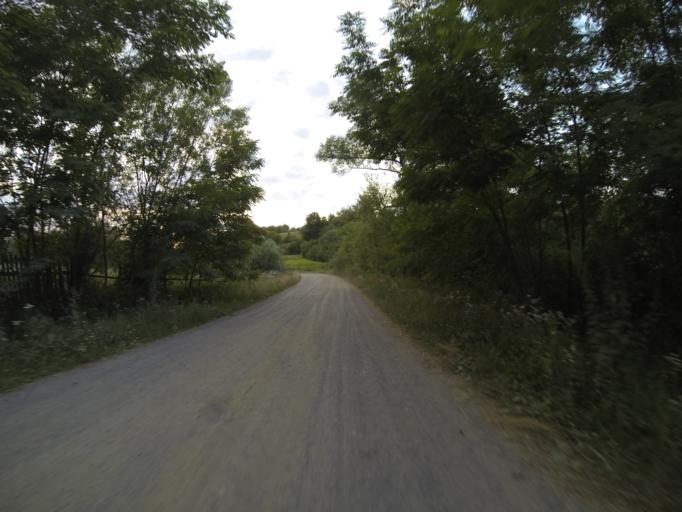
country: RO
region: Brasov
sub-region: Comuna Sinca Noua
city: Sinca Noua
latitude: 45.7130
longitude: 25.2573
